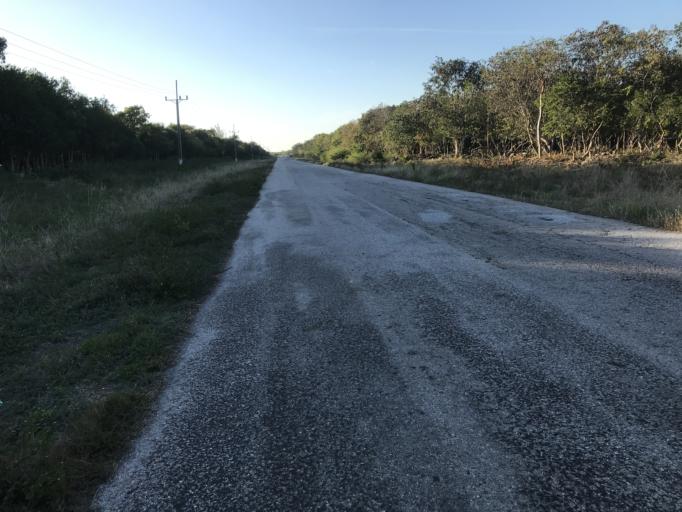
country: CU
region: Cienfuegos
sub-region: Municipio de Aguada de Pasajeros
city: Aguada de Pasajeros
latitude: 22.0762
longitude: -81.0624
